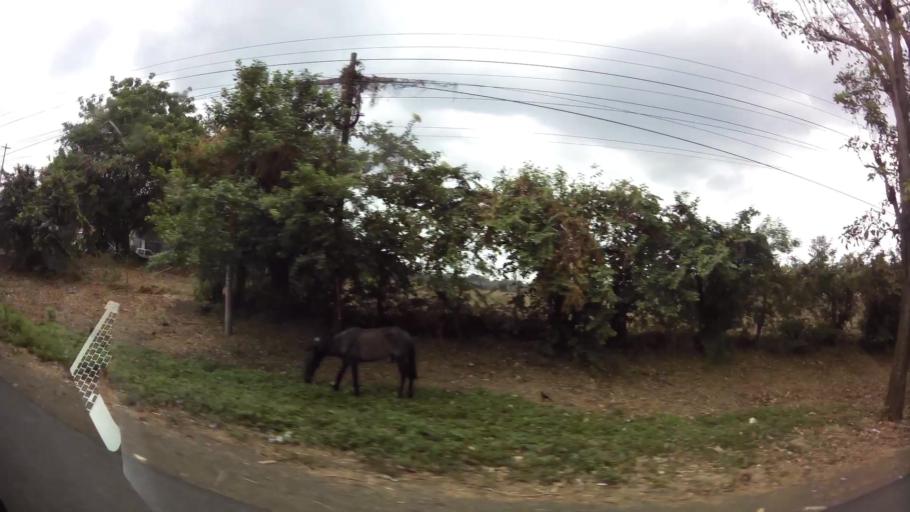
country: NI
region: Leon
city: Leon
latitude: 12.4746
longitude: -86.8634
